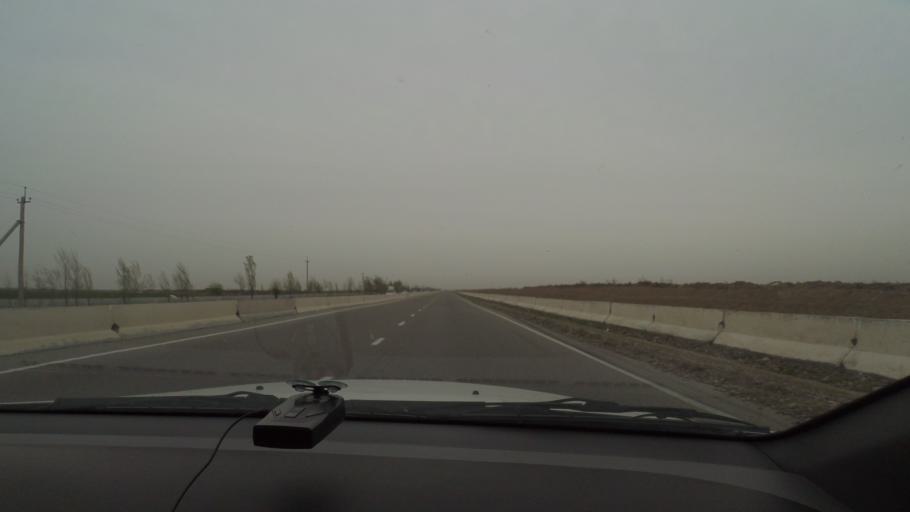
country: UZ
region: Jizzax
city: Dustlik
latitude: 40.4284
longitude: 68.2228
